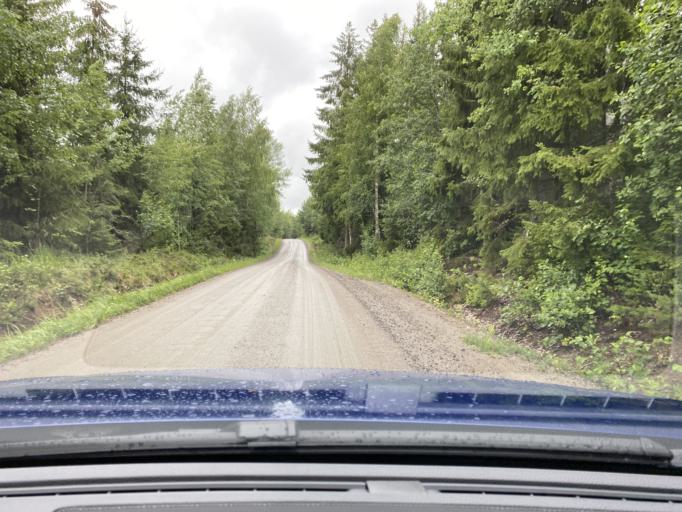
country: FI
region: Pirkanmaa
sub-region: Lounais-Pirkanmaa
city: Punkalaidun
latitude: 61.1460
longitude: 23.2689
